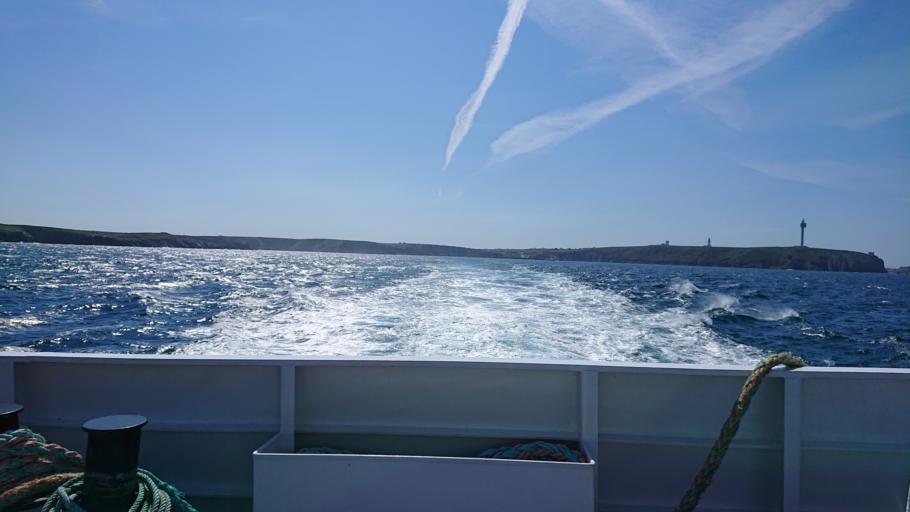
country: FR
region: Brittany
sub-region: Departement du Finistere
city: Porspoder
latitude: 48.4705
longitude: -5.0293
